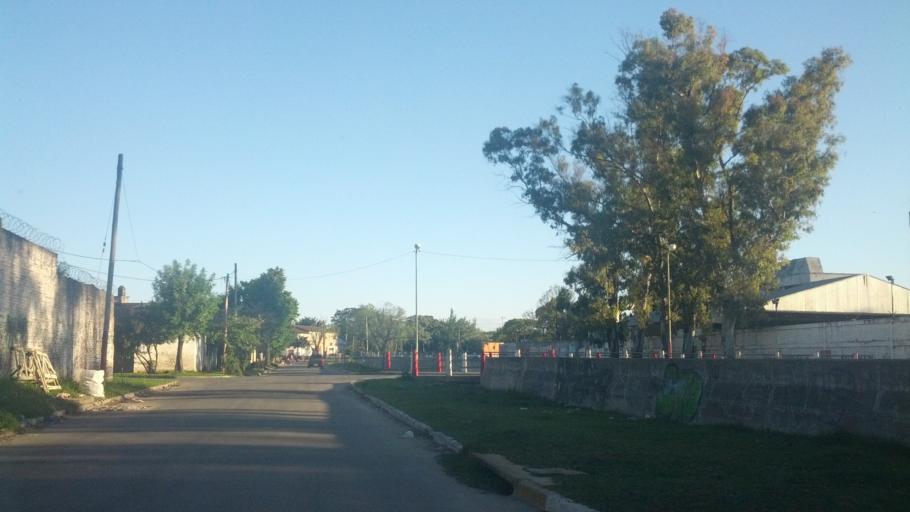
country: AR
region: Buenos Aires
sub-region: Partido de Lomas de Zamora
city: Lomas de Zamora
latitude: -34.7636
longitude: -58.4285
